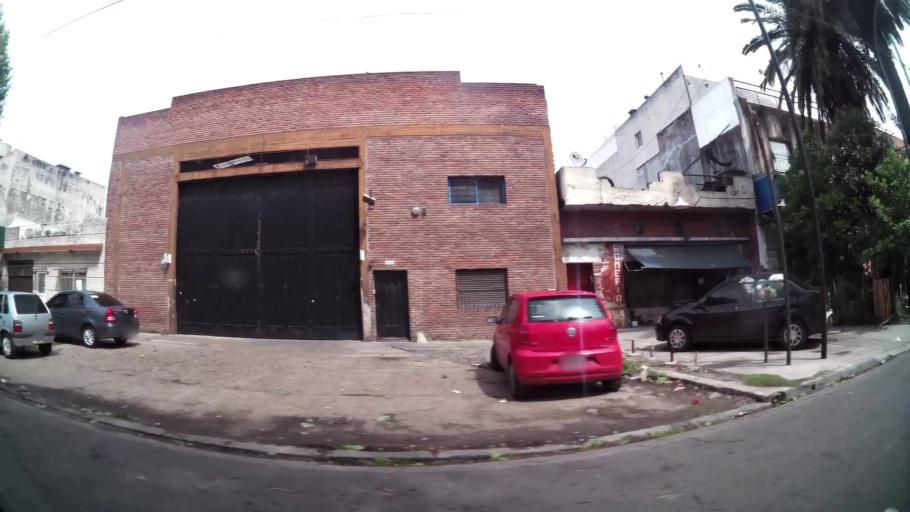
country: AR
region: Buenos Aires F.D.
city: Villa Lugano
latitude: -34.6599
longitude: -58.4278
